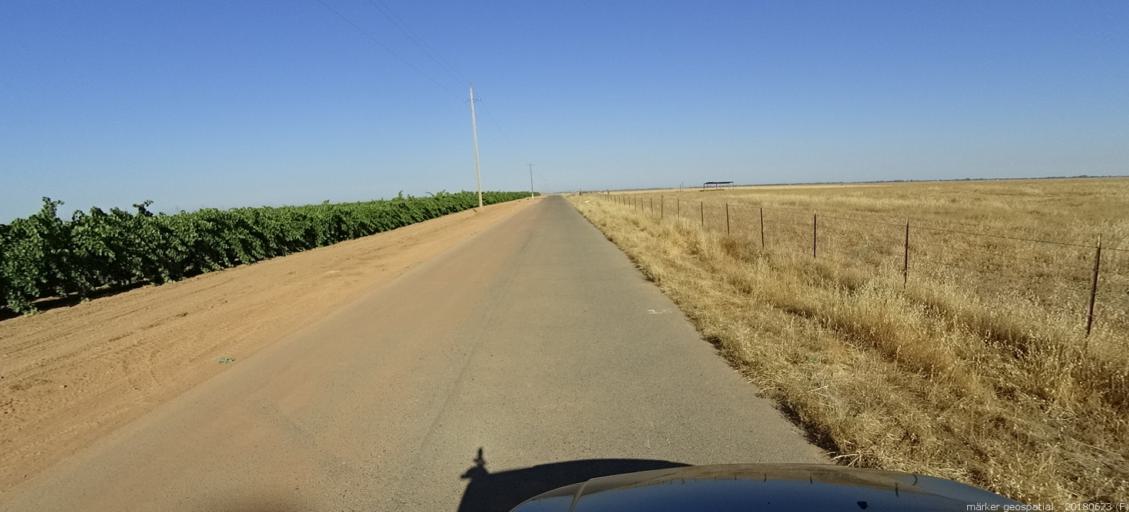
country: US
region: California
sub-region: Madera County
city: Bonadelle Ranchos-Madera Ranchos
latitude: 36.9521
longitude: -119.8060
